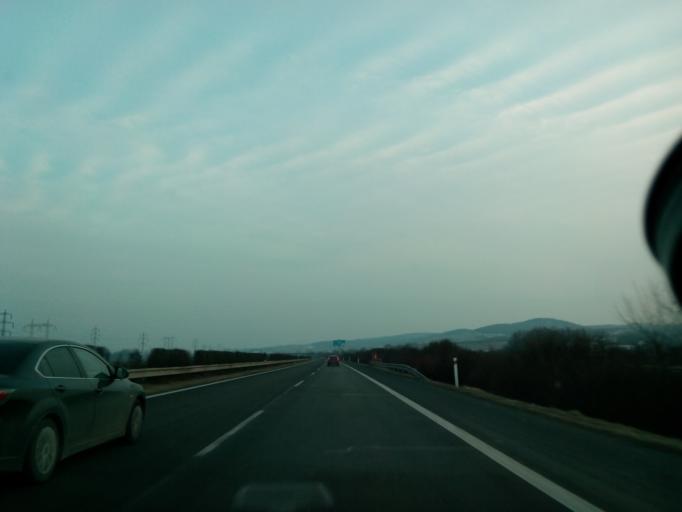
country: SK
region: Presovsky
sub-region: Okres Presov
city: Presov
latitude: 48.8850
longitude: 21.2497
